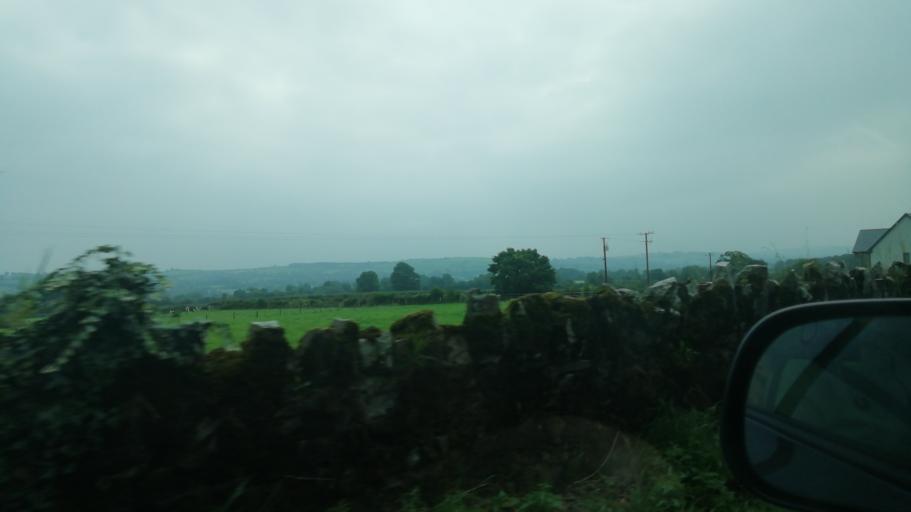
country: IE
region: Munster
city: Fethard
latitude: 52.5524
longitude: -7.6718
